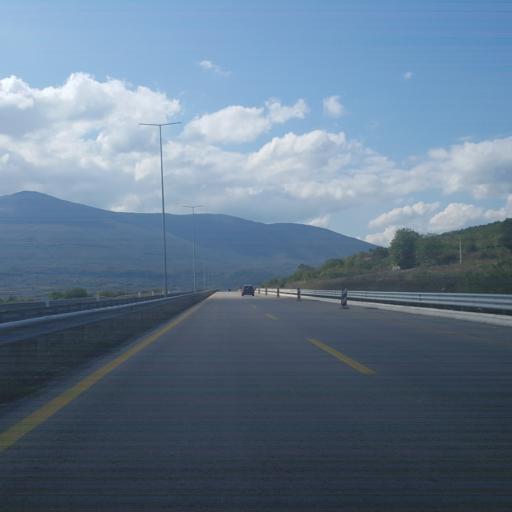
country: RS
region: Central Serbia
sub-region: Pirotski Okrug
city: Bela Palanka
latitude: 43.2366
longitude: 22.3252
